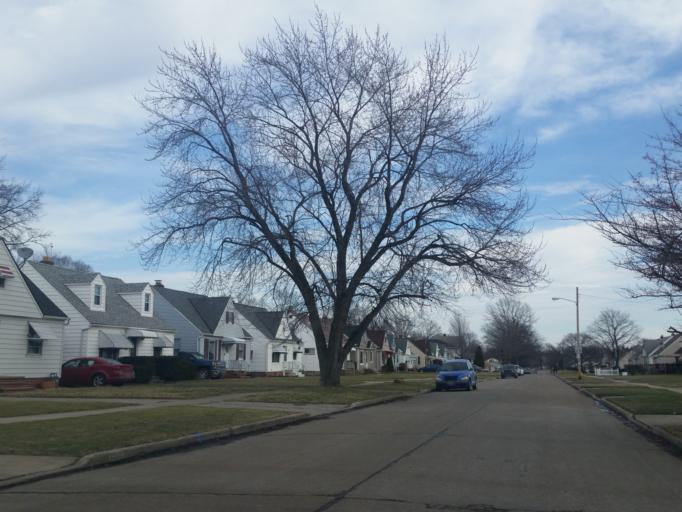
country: US
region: Ohio
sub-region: Cuyahoga County
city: Brooklyn Heights
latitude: 41.4151
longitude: -81.7018
